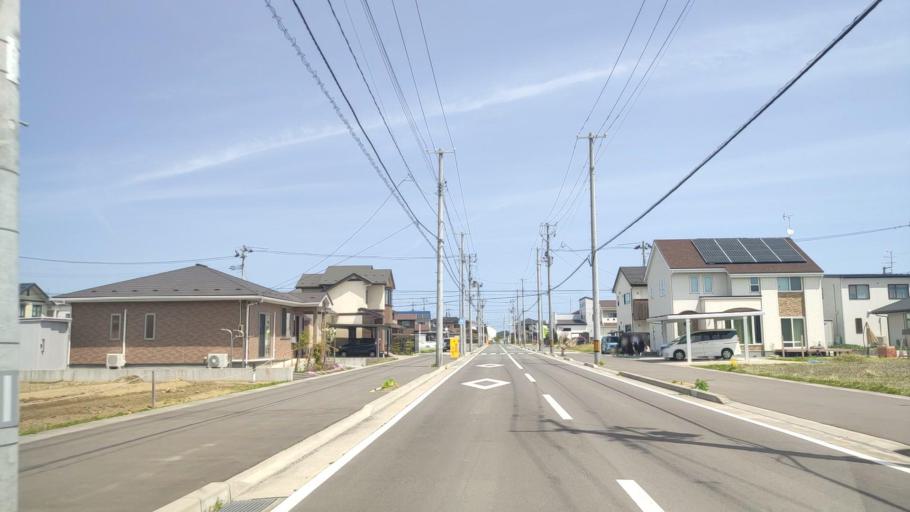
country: JP
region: Aomori
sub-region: Hachinohe Shi
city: Uchimaru
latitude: 40.5132
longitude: 141.4300
